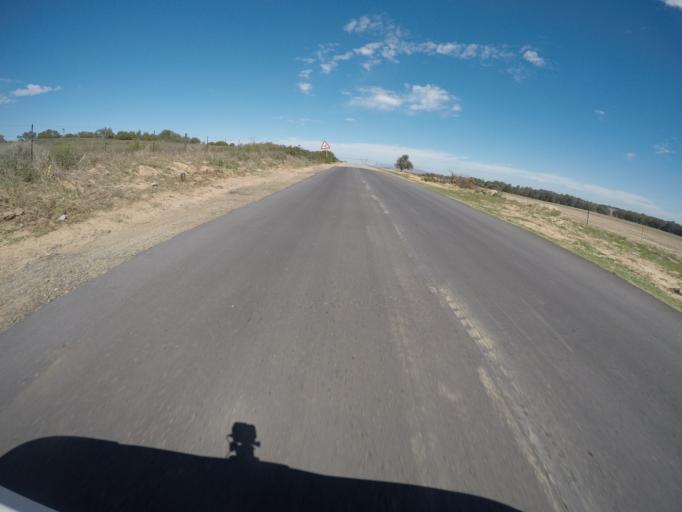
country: ZA
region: Western Cape
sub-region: West Coast District Municipality
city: Malmesbury
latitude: -33.5899
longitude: 18.6461
